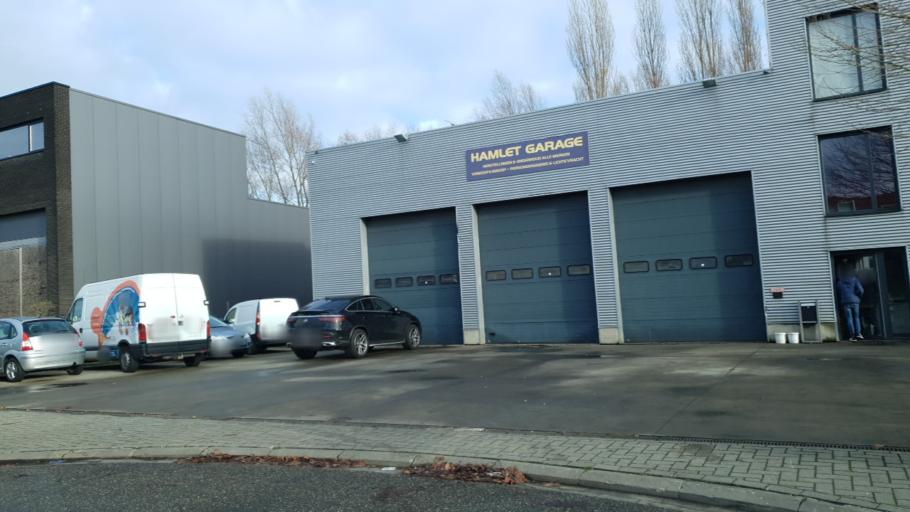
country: BE
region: Flanders
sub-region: Provincie Antwerpen
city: Lier
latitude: 51.1446
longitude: 4.5624
